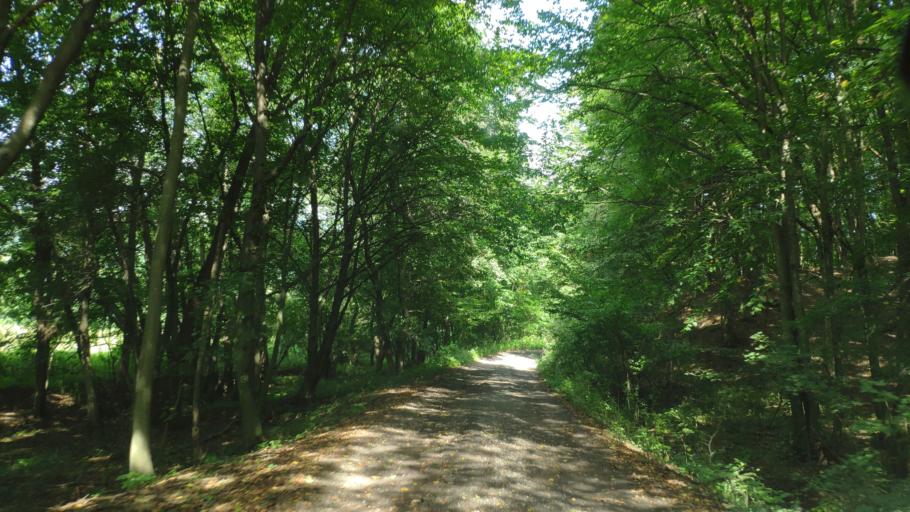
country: HU
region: Borsod-Abauj-Zemplen
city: Putnok
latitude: 48.4533
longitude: 20.3829
